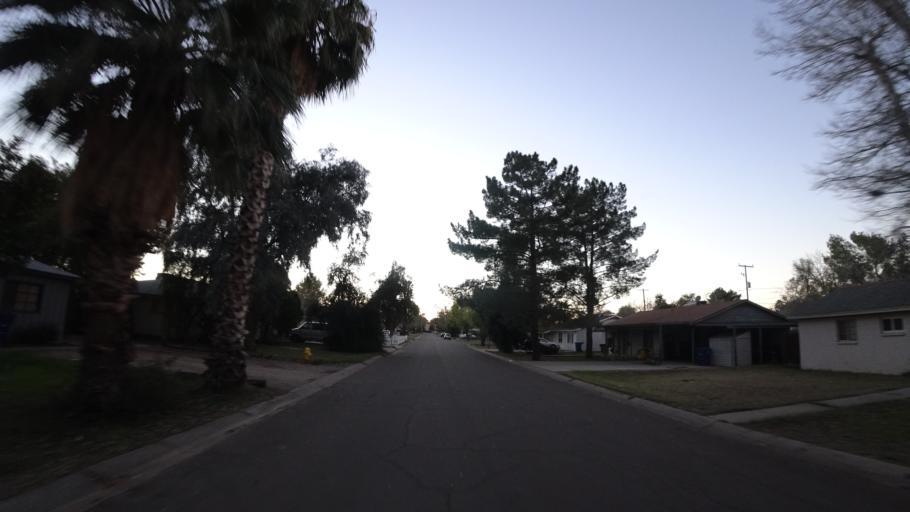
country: US
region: Arizona
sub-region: Maricopa County
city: Tempe Junction
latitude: 33.4139
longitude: -111.9451
